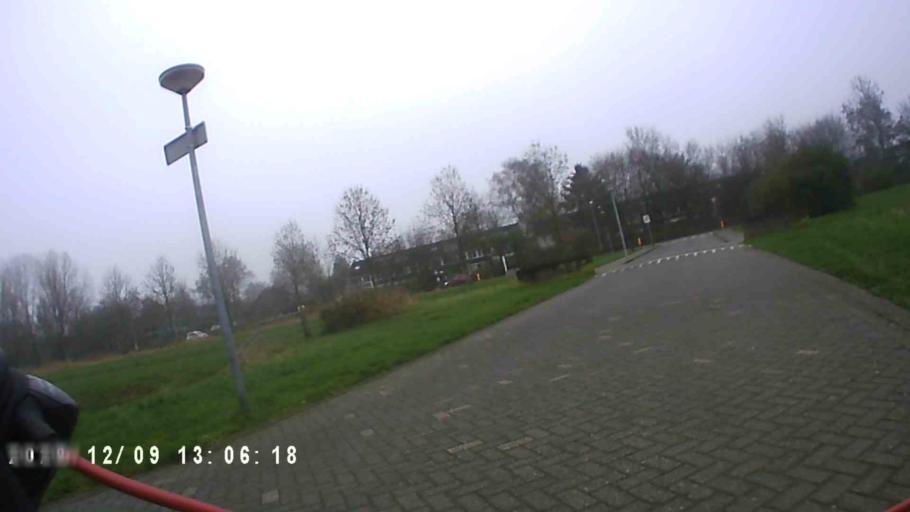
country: NL
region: Groningen
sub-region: Gemeente Groningen
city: Oosterpark
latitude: 53.2423
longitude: 6.6217
